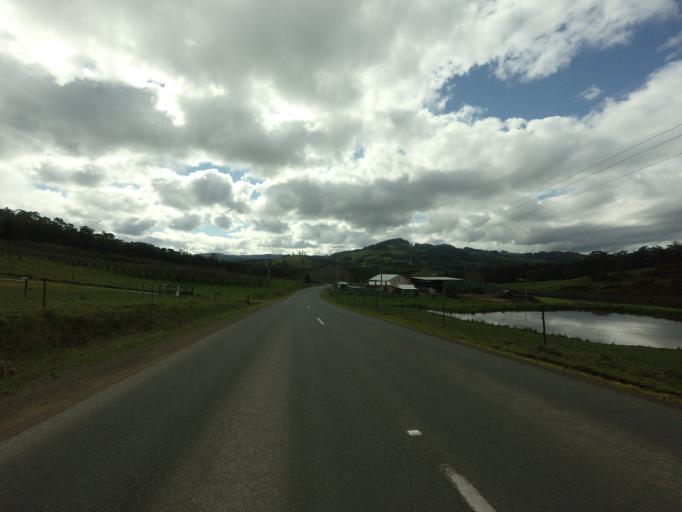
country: AU
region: Tasmania
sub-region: Huon Valley
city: Geeveston
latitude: -43.1744
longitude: 146.9459
